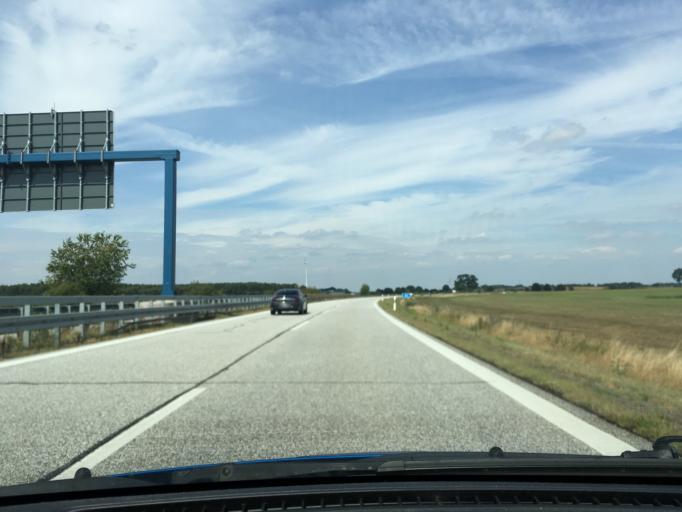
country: DE
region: Mecklenburg-Vorpommern
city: Mirow
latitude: 53.4367
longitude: 11.5056
